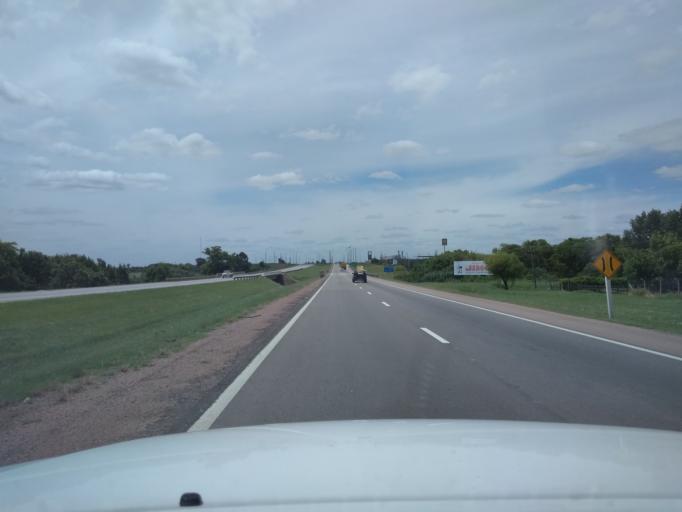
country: UY
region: Canelones
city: La Paz
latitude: -34.7553
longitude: -56.2584
